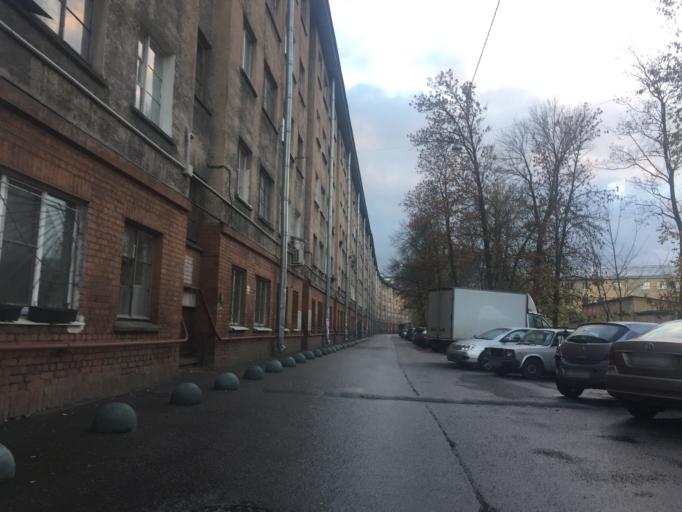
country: RU
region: St.-Petersburg
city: Obukhovo
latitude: 59.8801
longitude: 30.4379
